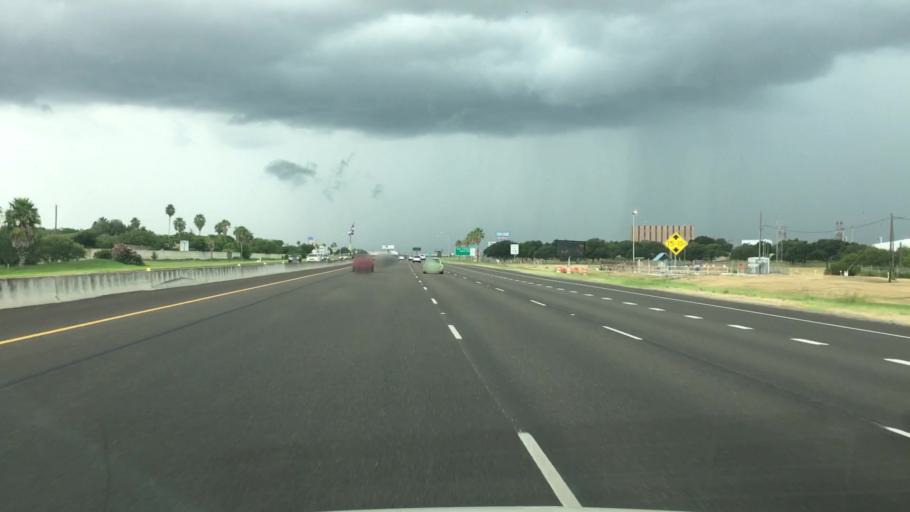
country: US
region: Texas
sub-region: Nueces County
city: Corpus Christi
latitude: 27.8046
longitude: -97.4769
